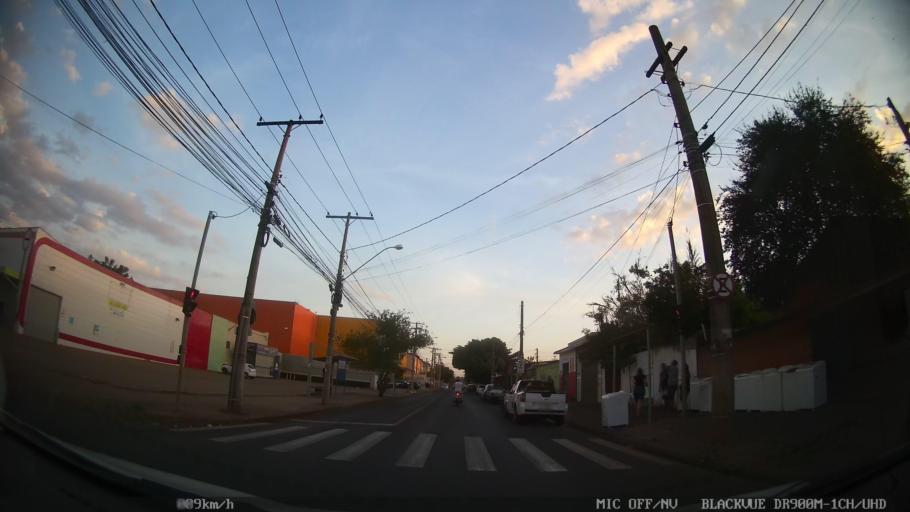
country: BR
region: Sao Paulo
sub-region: Ribeirao Preto
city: Ribeirao Preto
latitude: -21.1319
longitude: -47.8147
